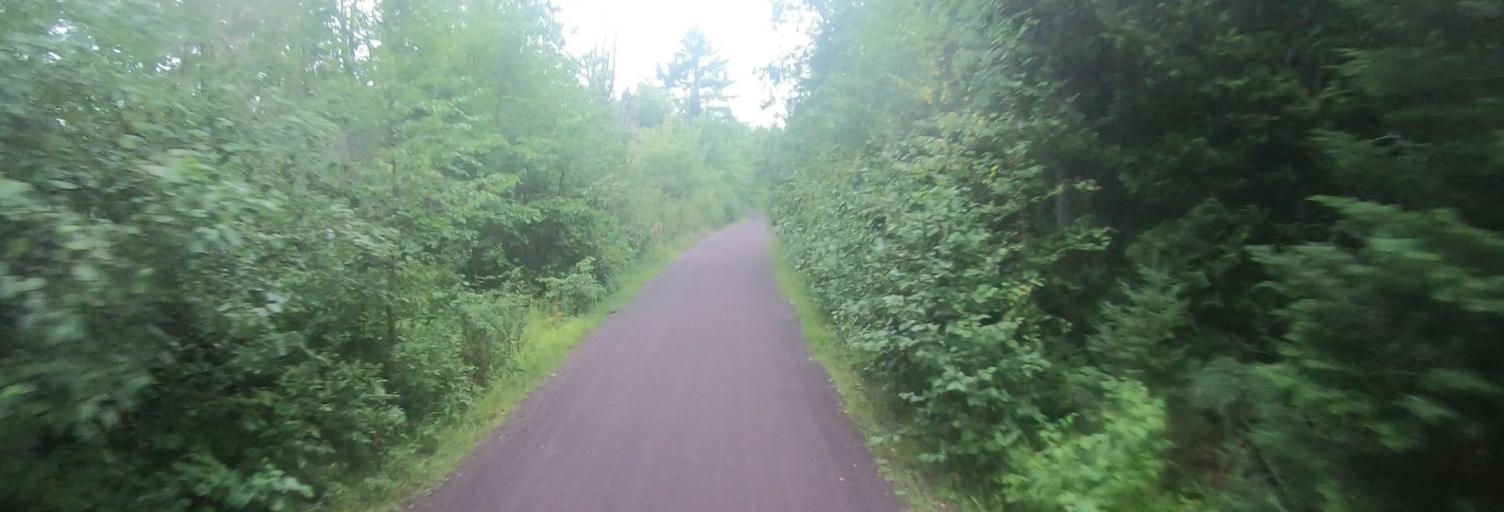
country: US
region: Michigan
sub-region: Keweenaw County
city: Eagle River
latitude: 47.2784
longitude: -88.2569
